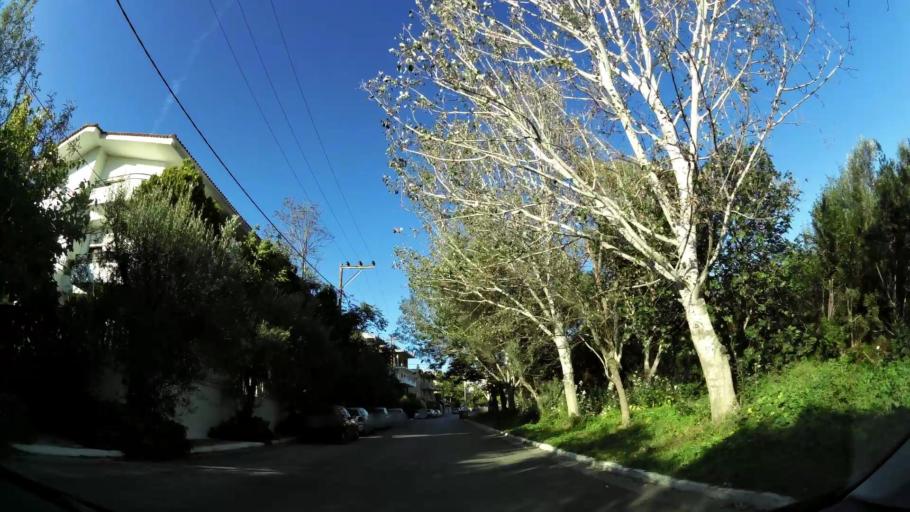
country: GR
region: Attica
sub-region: Nomarchia Anatolikis Attikis
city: Rafina
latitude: 38.0203
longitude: 23.9993
